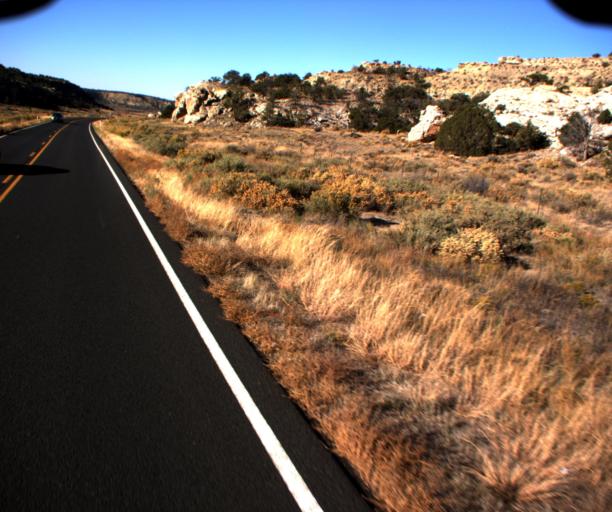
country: US
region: Arizona
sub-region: Apache County
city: Ganado
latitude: 35.7634
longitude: -109.8061
